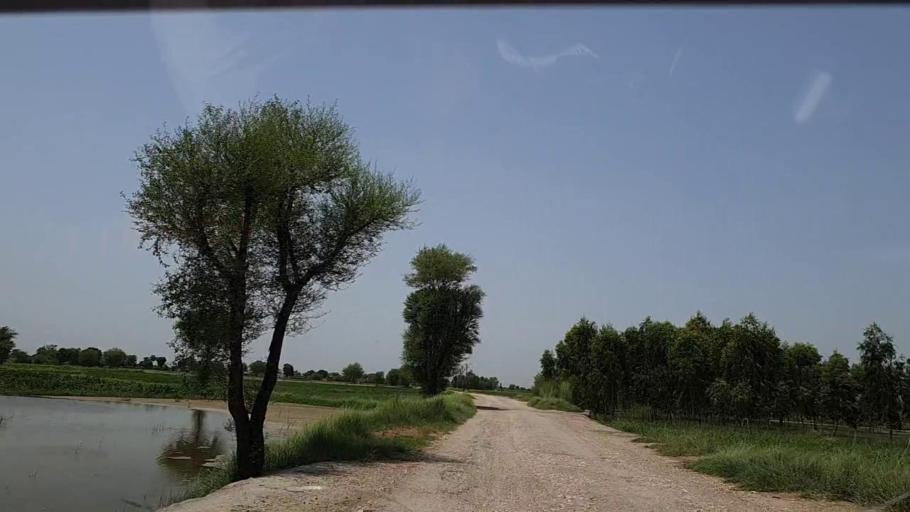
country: PK
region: Sindh
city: Tharu Shah
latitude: 26.9363
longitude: 68.0468
